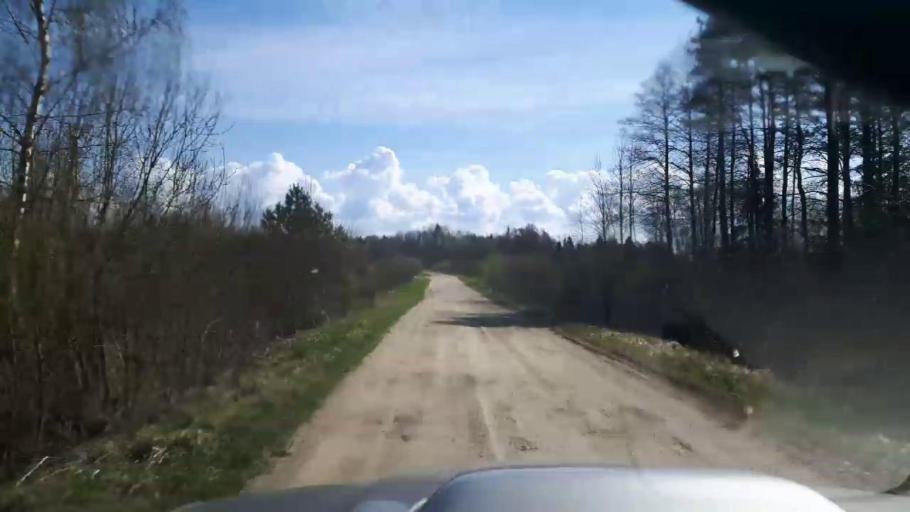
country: EE
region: Paernumaa
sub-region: Vaendra vald (alev)
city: Vandra
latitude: 58.5043
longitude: 24.9623
